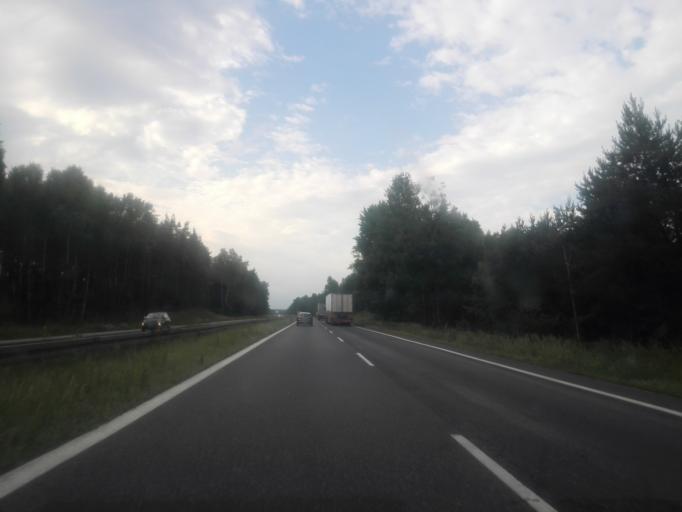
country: PL
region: Silesian Voivodeship
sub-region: Powiat bedzinski
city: Siewierz
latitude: 50.5235
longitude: 19.1927
